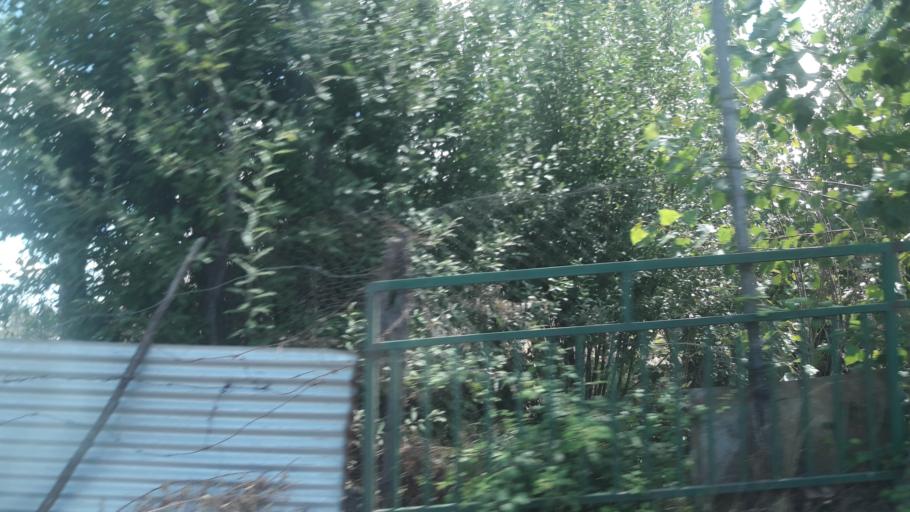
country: CL
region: Biobio
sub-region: Provincia de Biobio
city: Nacimiento
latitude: -37.5052
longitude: -72.6836
